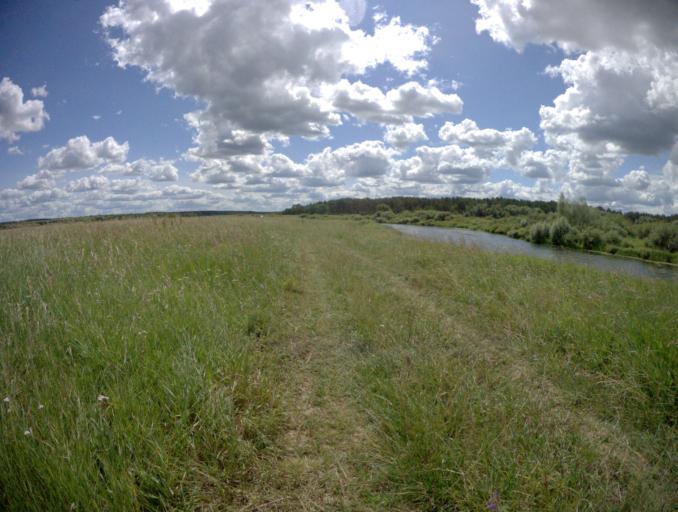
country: RU
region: Vladimir
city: Orgtrud
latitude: 56.3012
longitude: 40.6125
